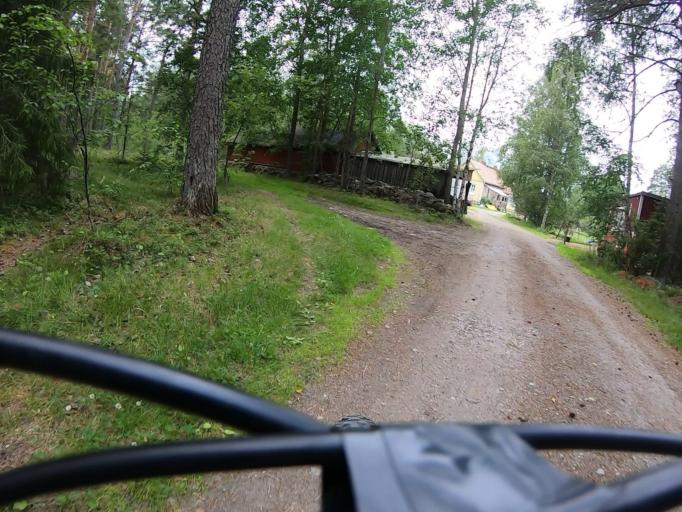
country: FI
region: Varsinais-Suomi
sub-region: Vakka-Suomi
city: Uusikaupunki
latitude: 60.8313
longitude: 21.4206
